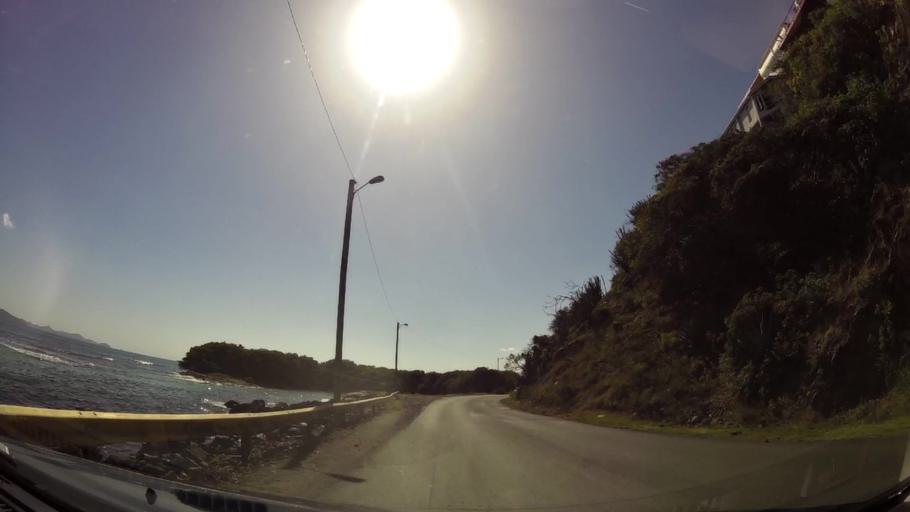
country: VG
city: Road Town
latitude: 18.4067
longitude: -64.6168
